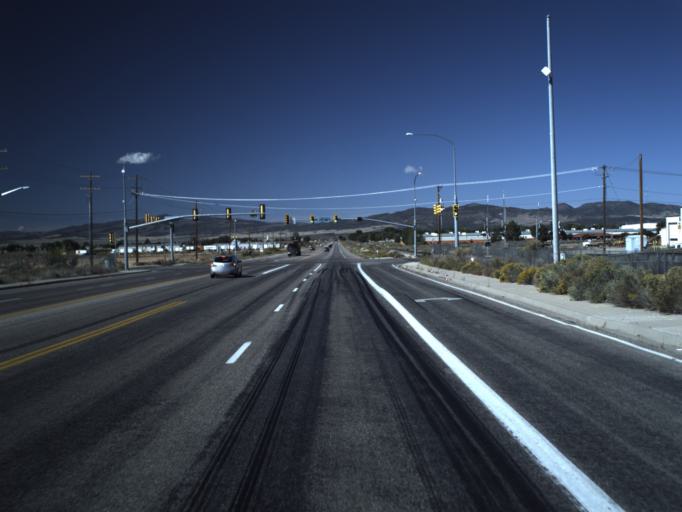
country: US
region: Utah
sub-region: Iron County
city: Cedar City
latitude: 37.6851
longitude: -113.1097
